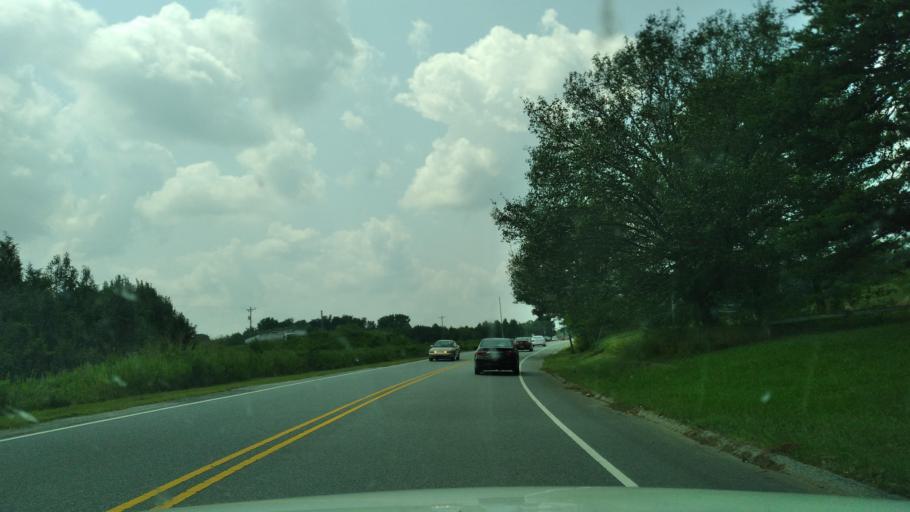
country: US
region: North Carolina
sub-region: Guilford County
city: Summerfield
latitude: 36.1242
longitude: -79.9003
